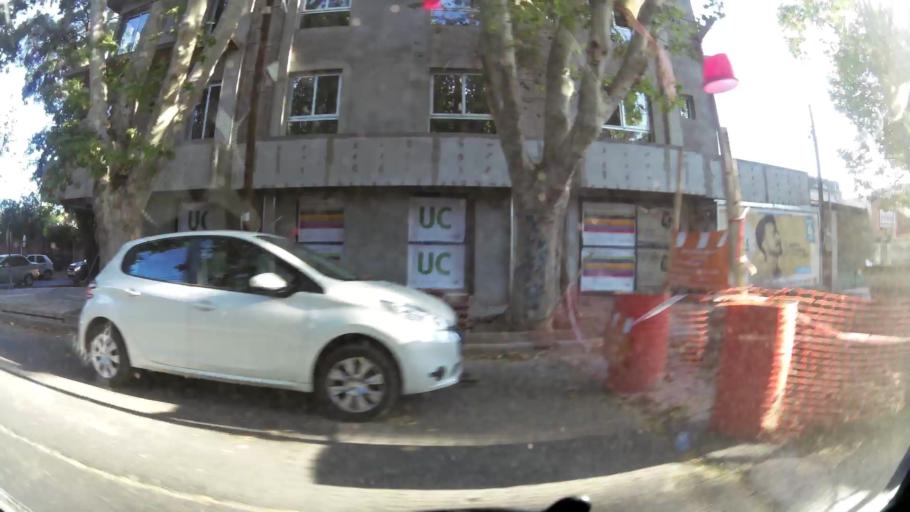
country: AR
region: Mendoza
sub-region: Departamento de Godoy Cruz
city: Godoy Cruz
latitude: -32.9079
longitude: -68.8465
